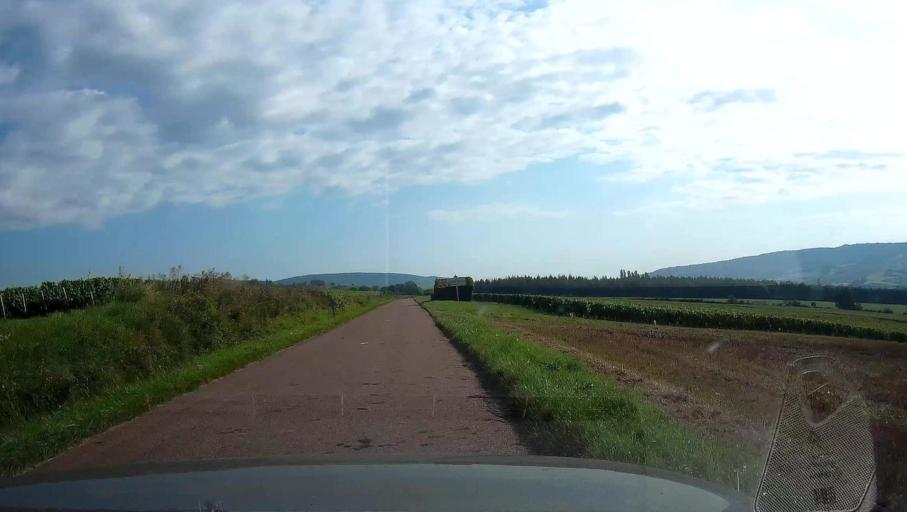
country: FR
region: Bourgogne
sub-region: Departement de Saone-et-Loire
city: Saint-Leger-sur-Dheune
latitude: 46.8813
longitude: 4.6406
